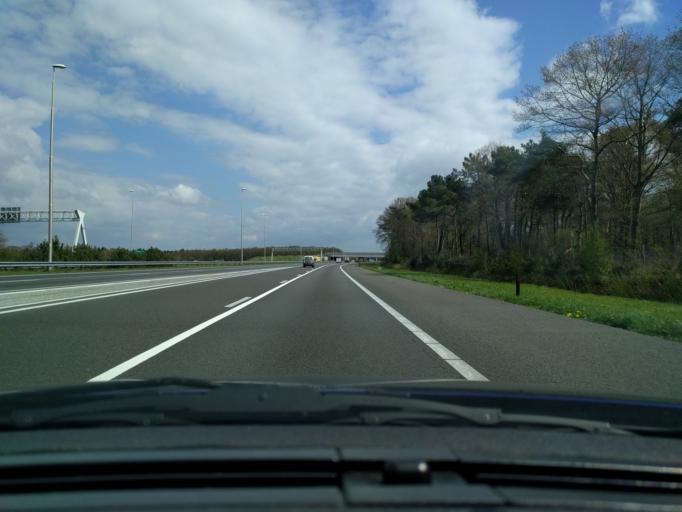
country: NL
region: North Brabant
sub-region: Gemeente Oss
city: Berghem
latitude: 51.7407
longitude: 5.5853
